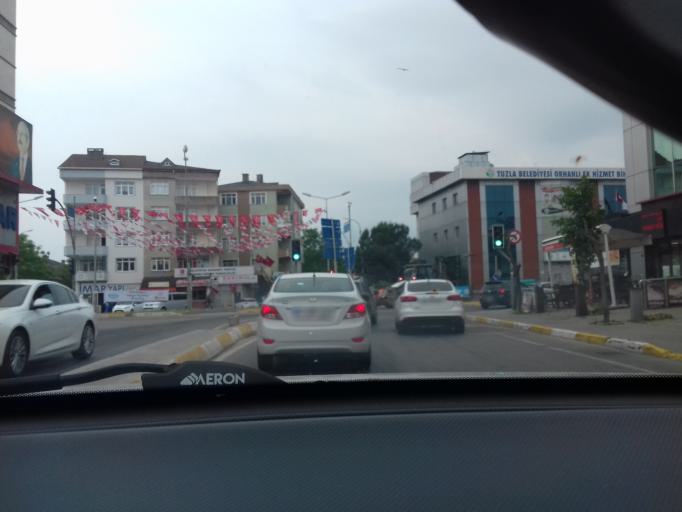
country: TR
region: Istanbul
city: Icmeler
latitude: 40.8965
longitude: 29.3564
